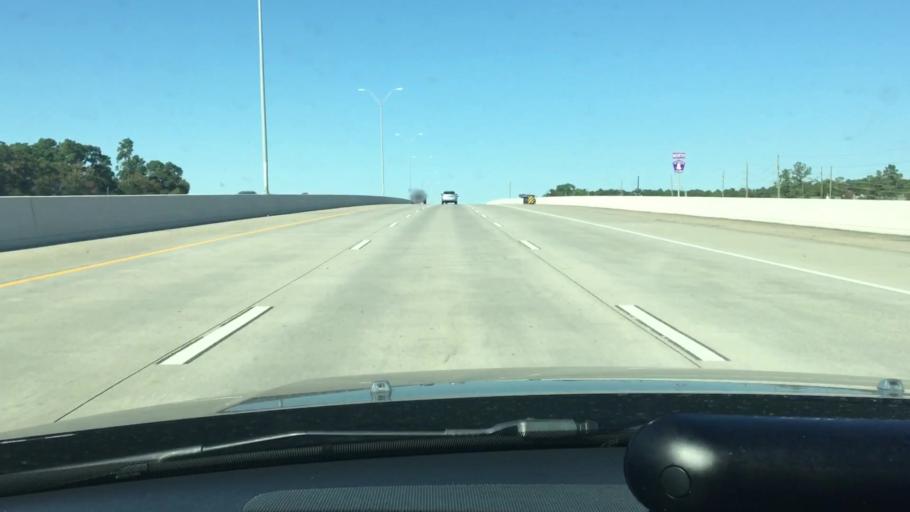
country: US
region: Texas
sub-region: Harris County
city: Sheldon
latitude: 29.8815
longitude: -95.1963
